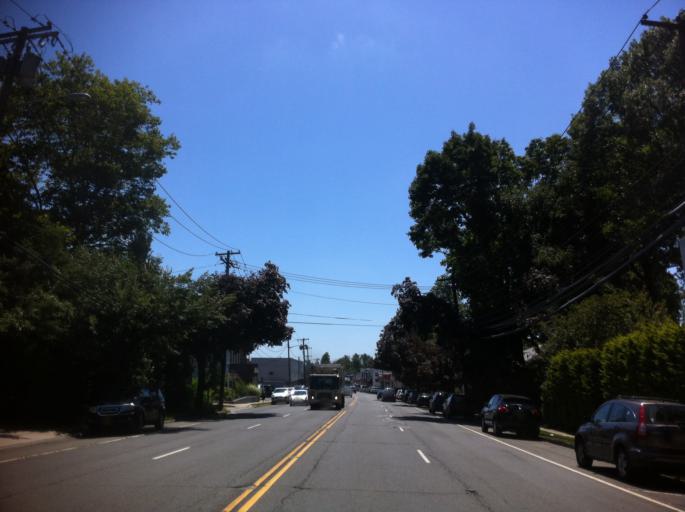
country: US
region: New York
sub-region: Nassau County
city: Roslyn Estates
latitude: 40.7925
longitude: -73.6536
